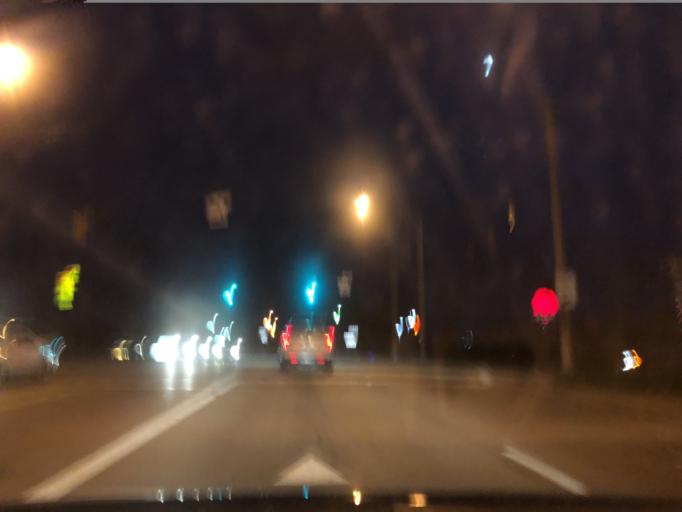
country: US
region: Ohio
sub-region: Hamilton County
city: Dillonvale
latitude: 39.2256
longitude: -84.3940
